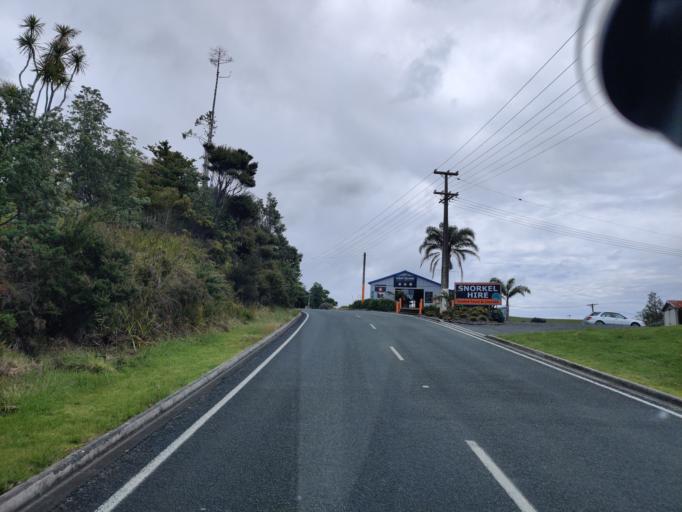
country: NZ
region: Auckland
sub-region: Auckland
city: Warkworth
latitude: -36.2892
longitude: 174.7983
